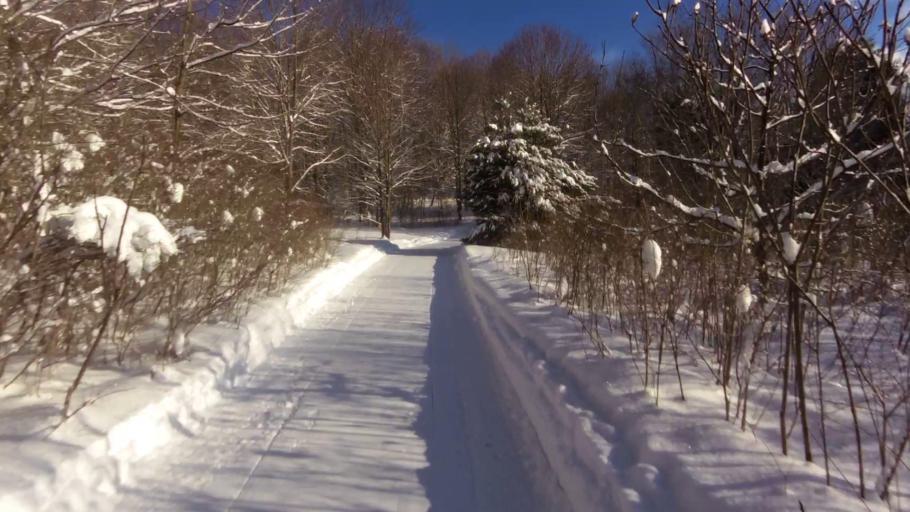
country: US
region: New York
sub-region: Chautauqua County
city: Falconer
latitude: 42.2562
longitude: -79.1650
